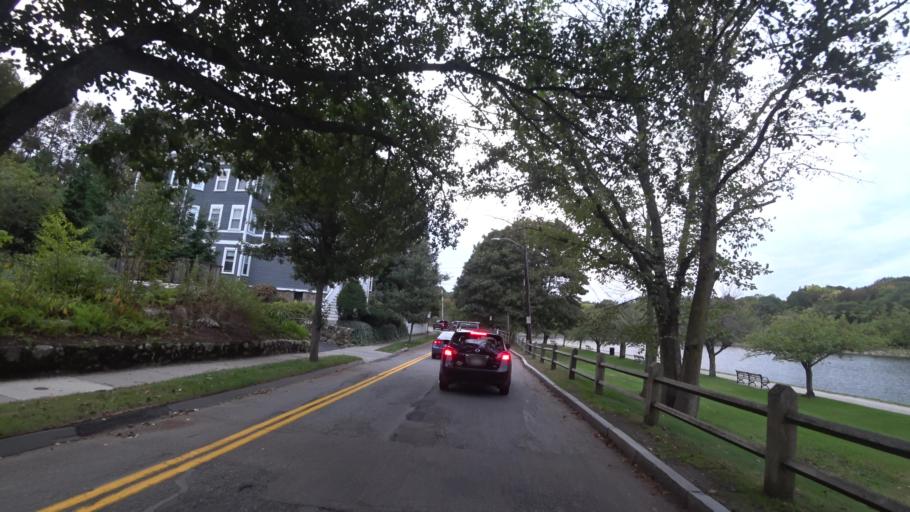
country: US
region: Massachusetts
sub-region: Norfolk County
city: Brookline
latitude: 42.3261
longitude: -71.1362
